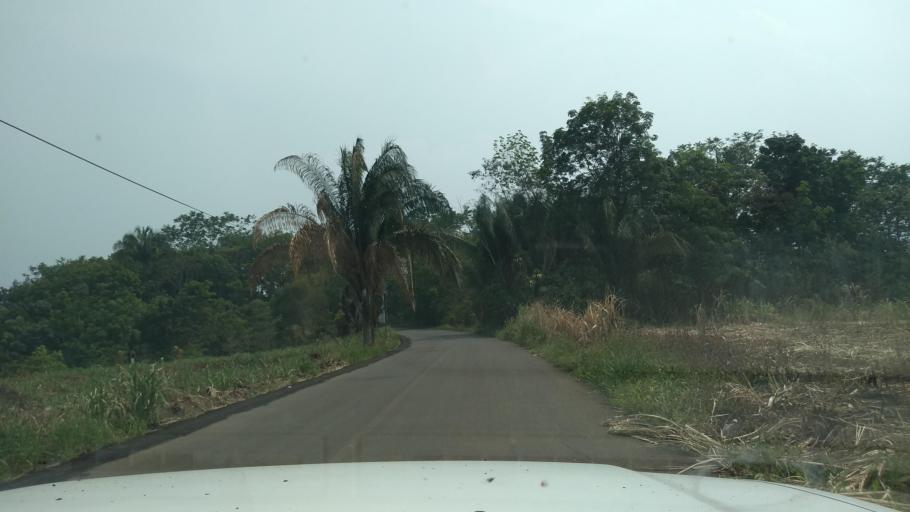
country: MX
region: Veracruz
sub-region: Tezonapa
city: Laguna Chica (Pueblo Nuevo)
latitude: 18.5343
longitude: -96.7869
